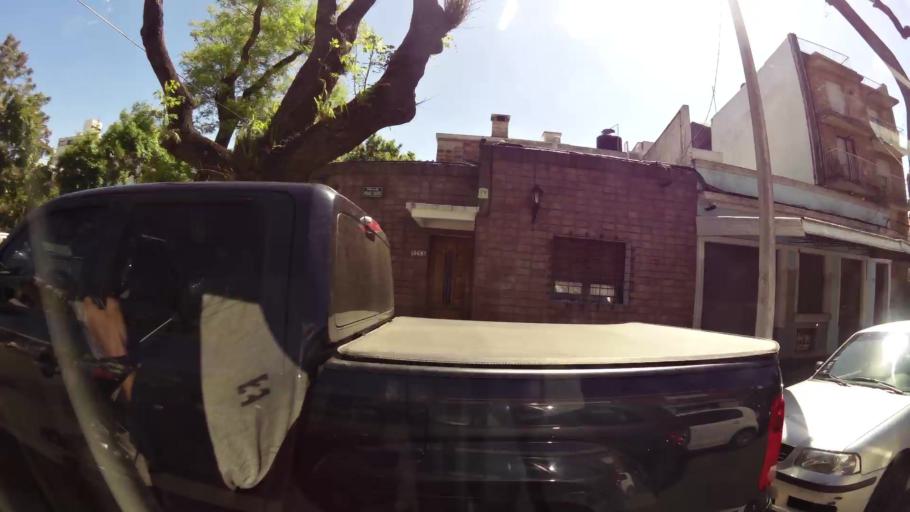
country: UY
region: Montevideo
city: Montevideo
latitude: -34.9049
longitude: -56.1387
